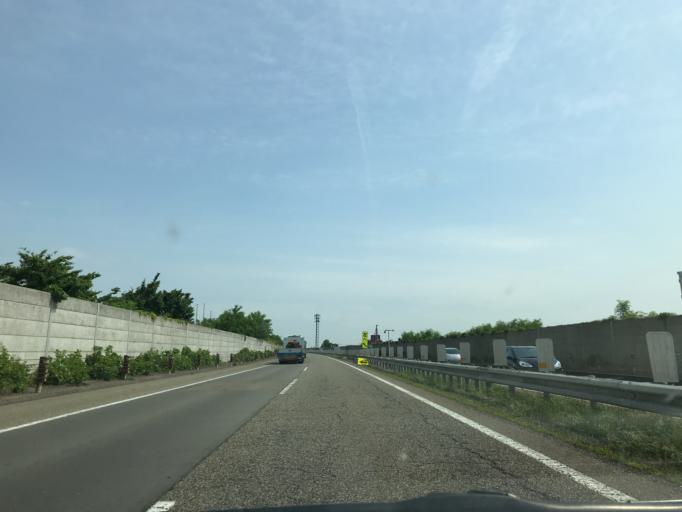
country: JP
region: Niigata
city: Sanjo
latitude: 37.6244
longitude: 138.9253
